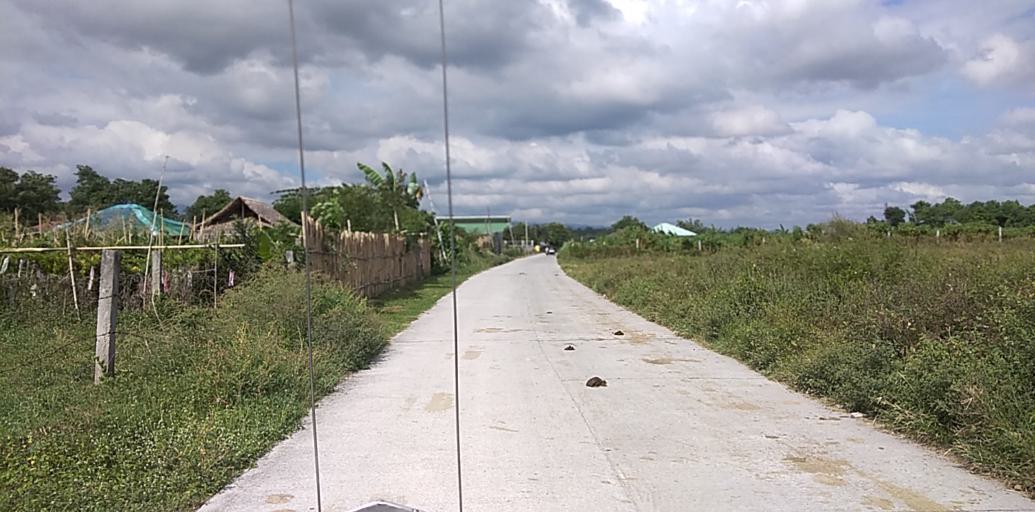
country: PH
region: Central Luzon
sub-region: Province of Pampanga
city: Porac
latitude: 15.0608
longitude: 120.5375
